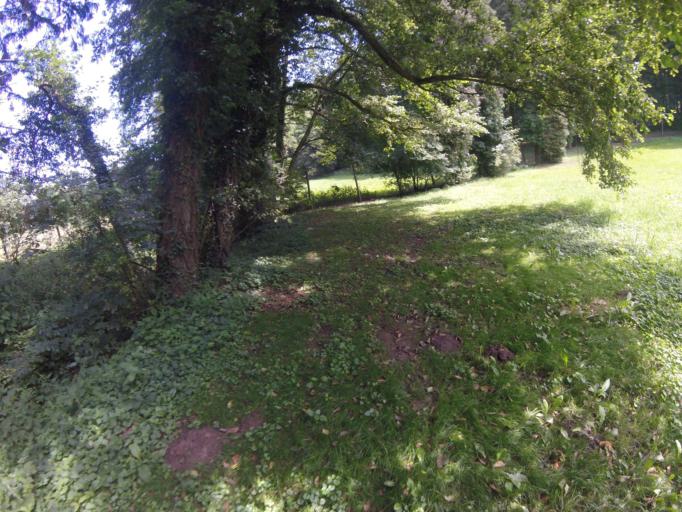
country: HU
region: Zala
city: Letenye
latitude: 46.5097
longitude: 16.7036
